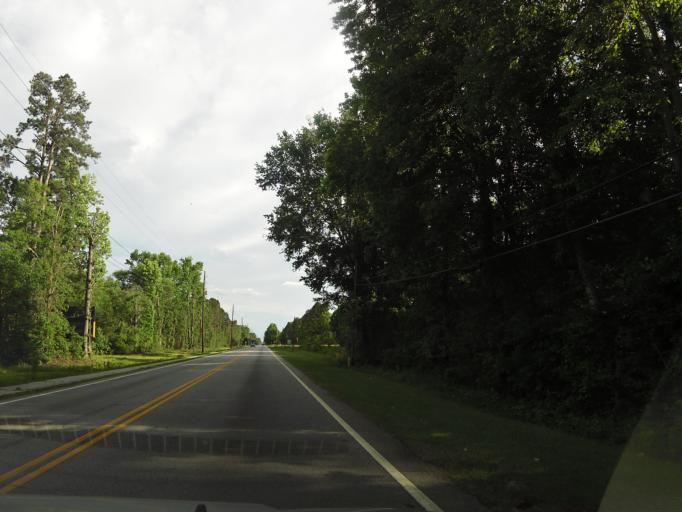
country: US
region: South Carolina
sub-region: Hampton County
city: Estill
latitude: 32.7427
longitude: -81.2416
